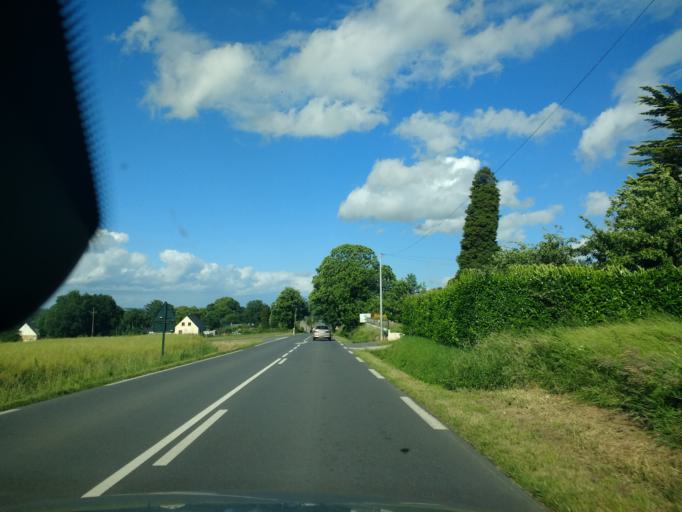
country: FR
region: Brittany
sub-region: Departement du Morbihan
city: La Gacilly
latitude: 47.7676
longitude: -2.1071
